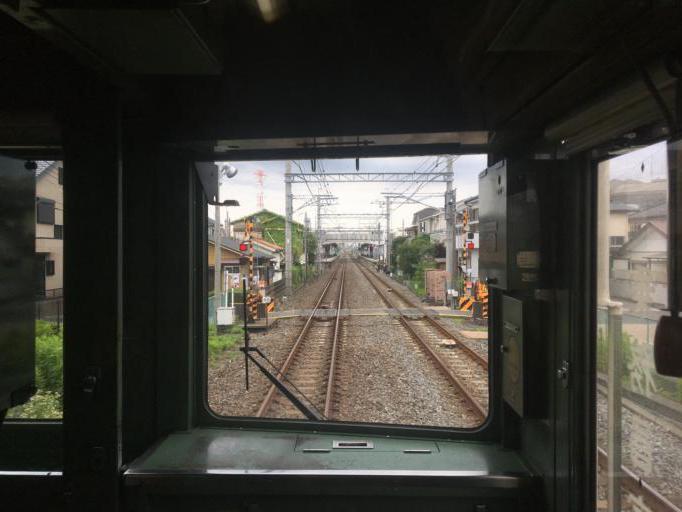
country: JP
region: Saitama
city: Kasukabe
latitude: 35.9796
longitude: 139.7438
